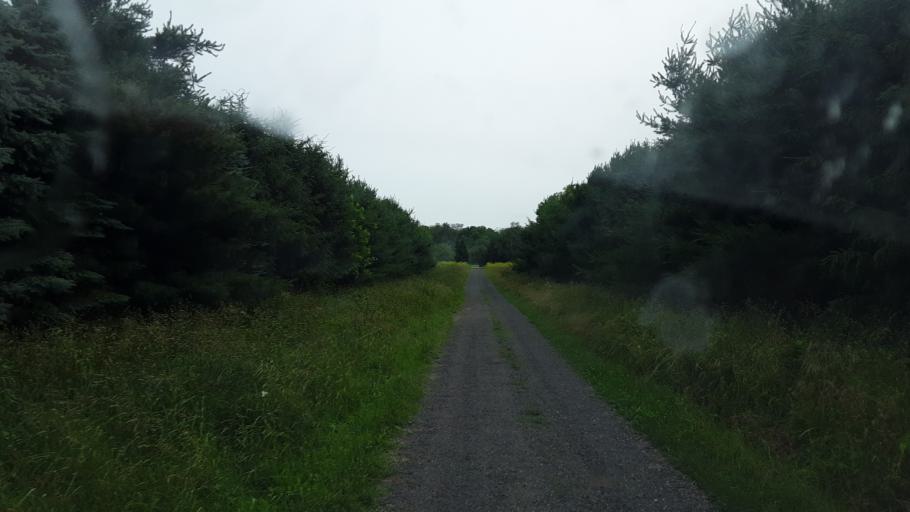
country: US
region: Ohio
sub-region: Crawford County
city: Galion
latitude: 40.6765
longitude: -82.8553
